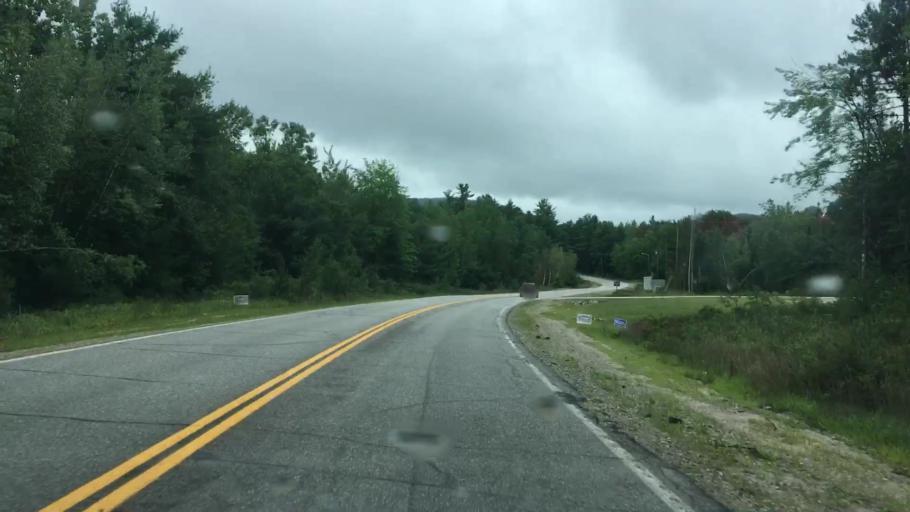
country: US
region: Maine
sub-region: Oxford County
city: Brownfield
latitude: 43.9868
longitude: -70.9324
